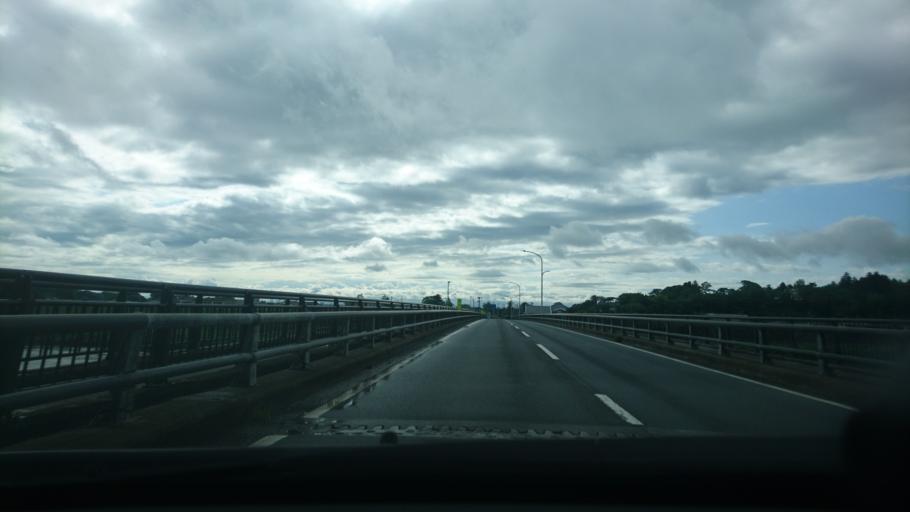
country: JP
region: Miyagi
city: Wakuya
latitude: 38.6529
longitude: 141.2864
